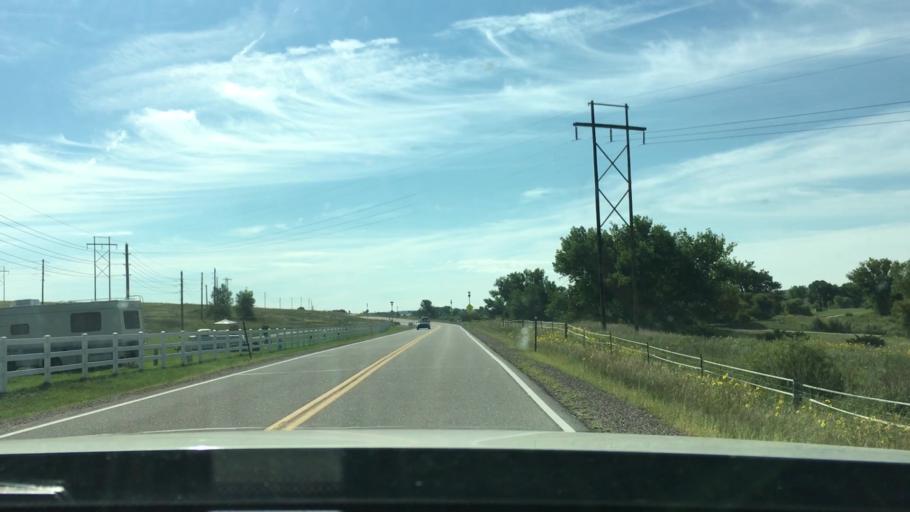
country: US
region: Colorado
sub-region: Douglas County
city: The Pinery
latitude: 39.4301
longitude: -104.7443
